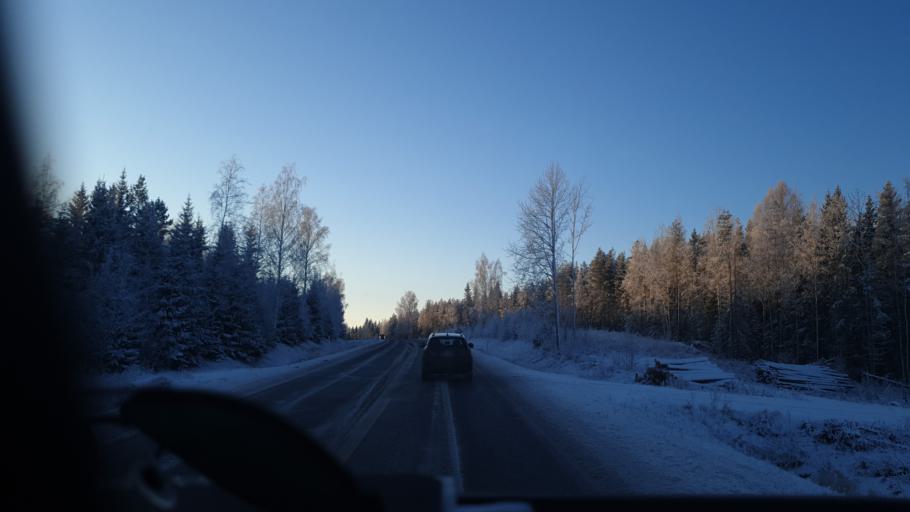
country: FI
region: Central Ostrobothnia
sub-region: Kokkola
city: Kaelviae
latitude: 63.9074
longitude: 23.3876
